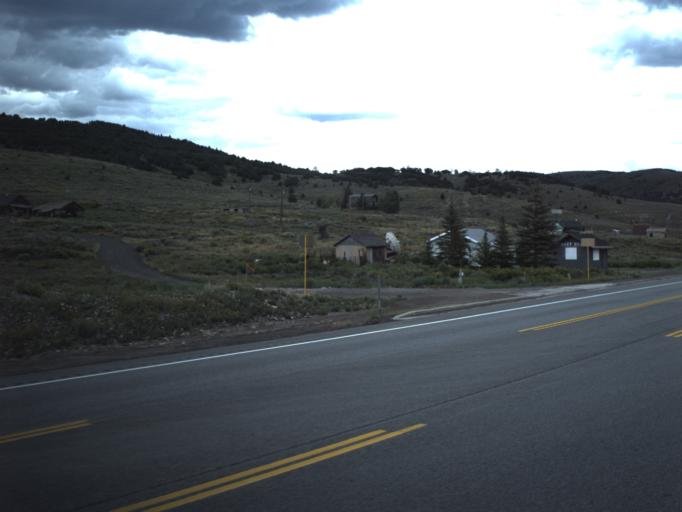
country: US
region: Utah
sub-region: Carbon County
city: Helper
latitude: 39.9285
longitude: -111.0833
